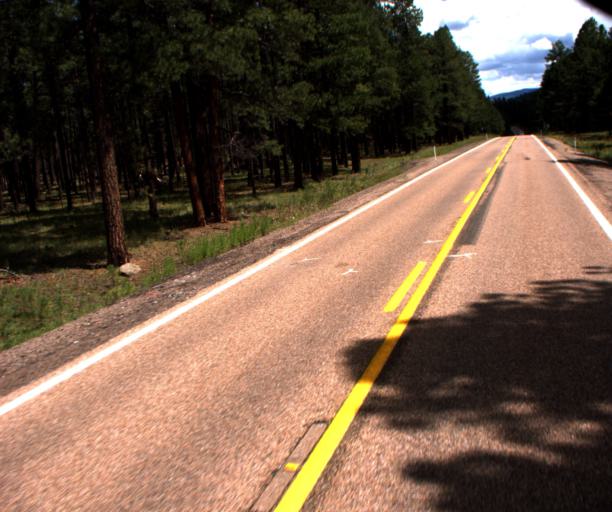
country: US
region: Arizona
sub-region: Navajo County
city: Pinetop-Lakeside
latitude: 34.0560
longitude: -109.7583
